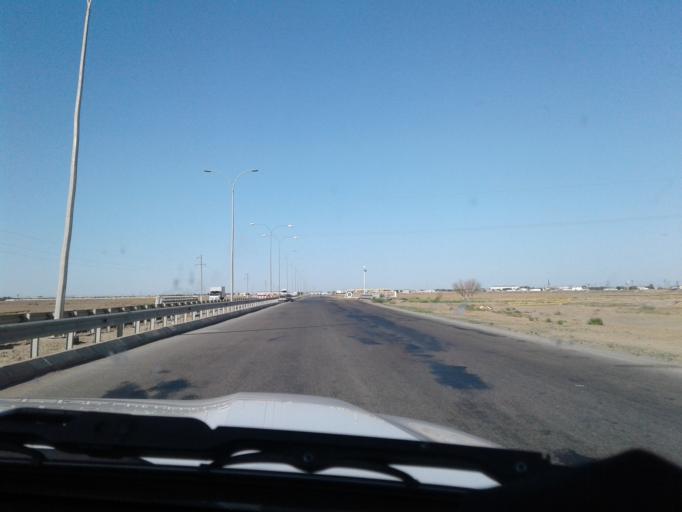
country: TM
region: Ahal
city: Tejen
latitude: 37.3710
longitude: 60.4635
